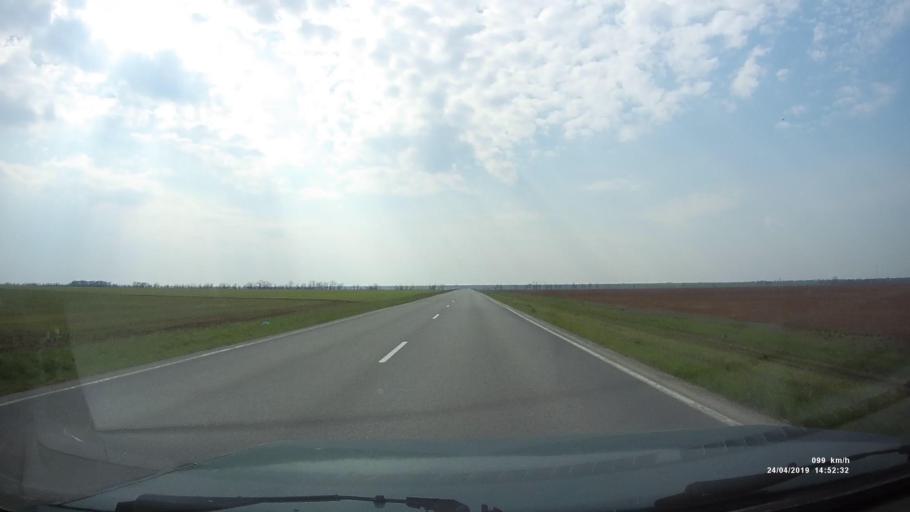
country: RU
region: Rostov
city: Remontnoye
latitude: 46.5304
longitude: 43.6788
